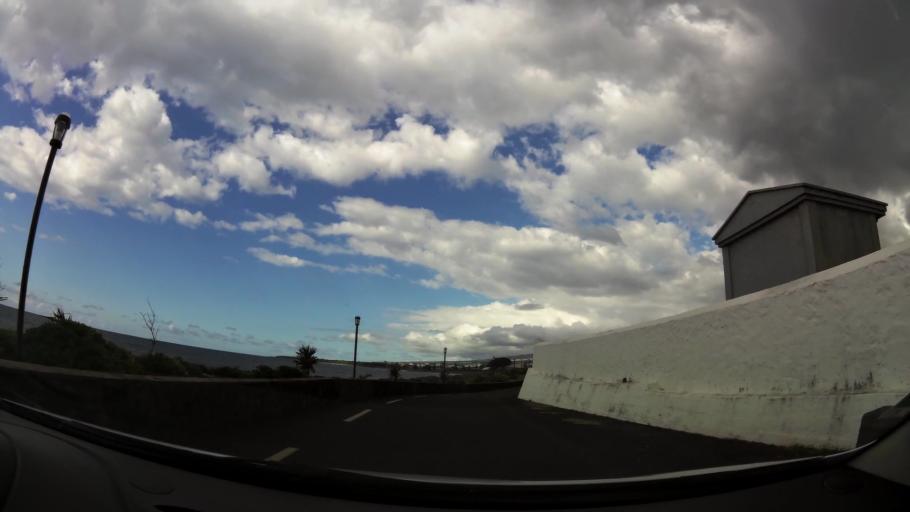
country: RE
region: Reunion
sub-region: Reunion
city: Saint-Denis
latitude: -20.8811
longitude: 55.4634
